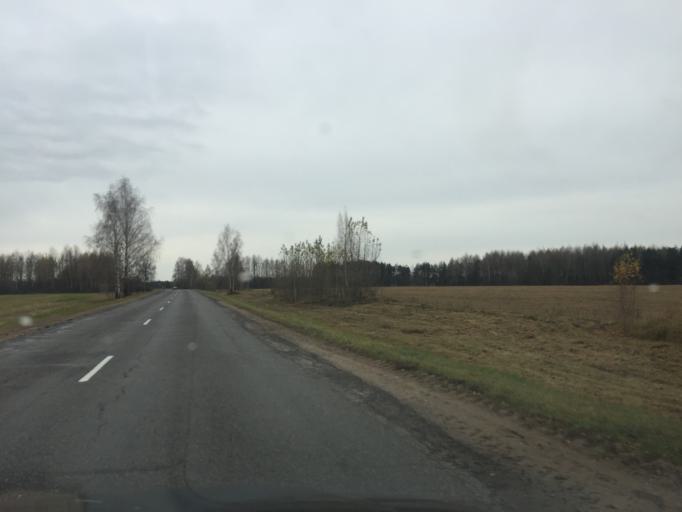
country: BY
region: Mogilev
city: Drybin
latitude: 54.1050
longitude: 31.0942
